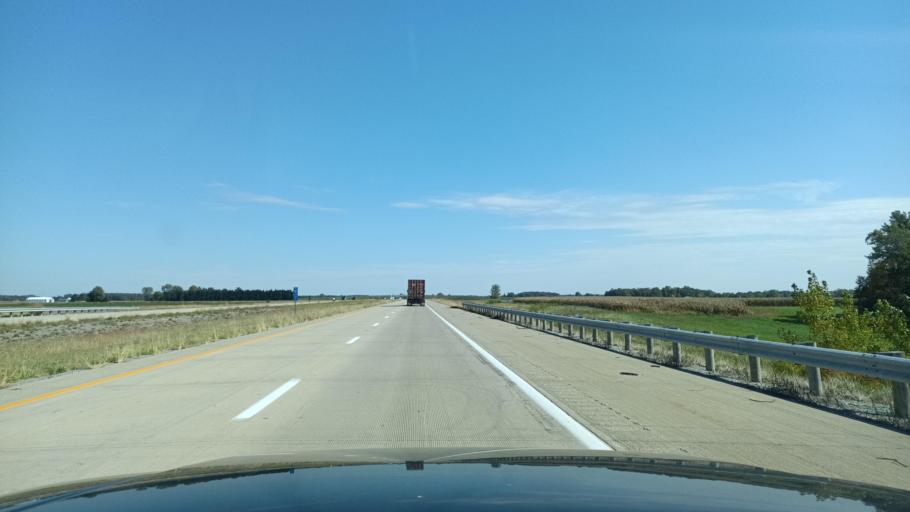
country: US
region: Ohio
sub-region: Henry County
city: Liberty Center
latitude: 41.4331
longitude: -83.9358
